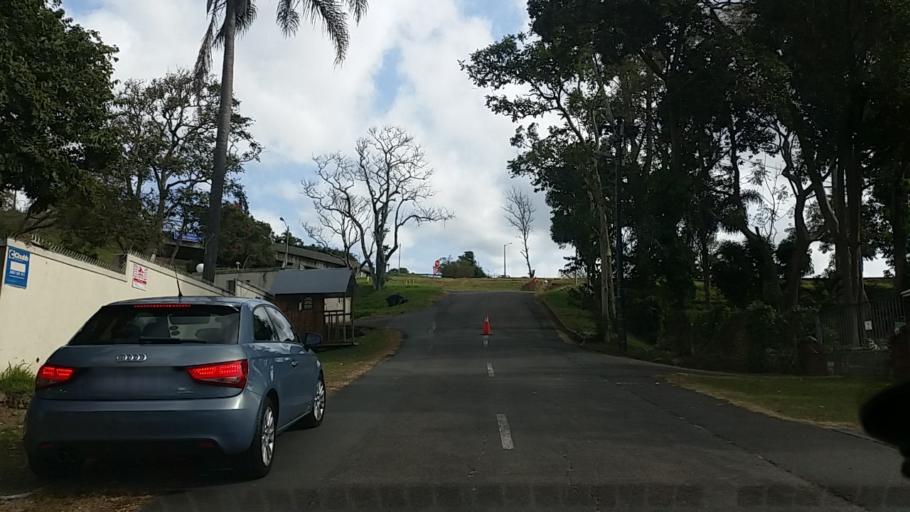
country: ZA
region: KwaZulu-Natal
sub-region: eThekwini Metropolitan Municipality
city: Berea
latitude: -29.8318
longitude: 30.9426
